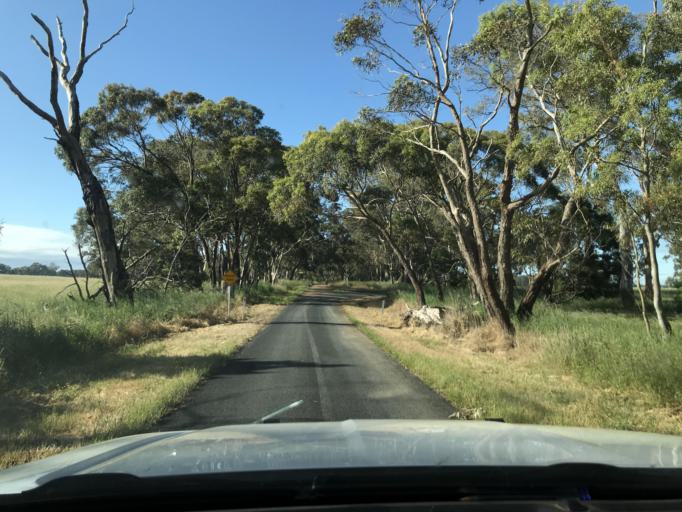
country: AU
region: South Australia
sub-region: Wattle Range
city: Penola
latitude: -37.2033
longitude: 140.9714
